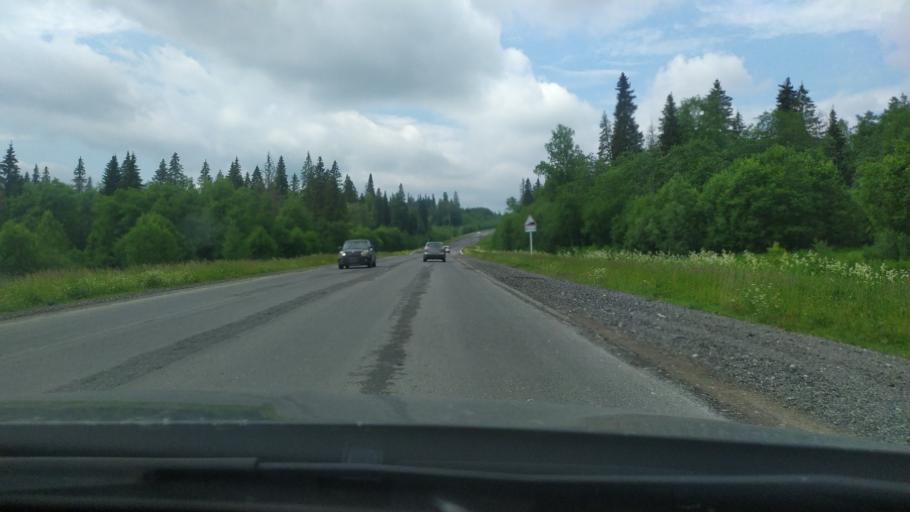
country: RU
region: Perm
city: Kalino
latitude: 58.2767
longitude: 57.3945
